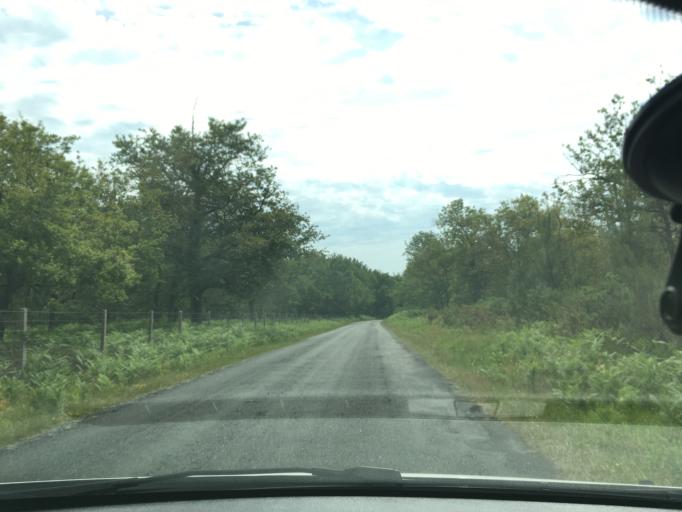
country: FR
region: Aquitaine
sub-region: Departement de la Gironde
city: Gaillan-en-Medoc
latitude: 45.3460
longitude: -1.0273
